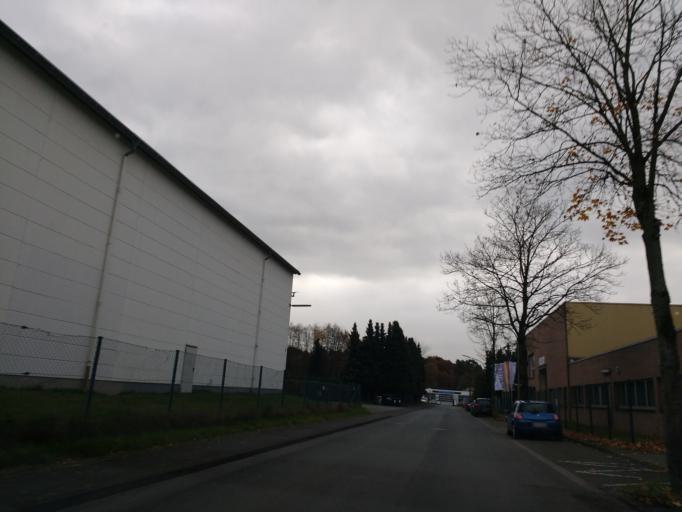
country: DE
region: North Rhine-Westphalia
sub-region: Regierungsbezirk Detmold
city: Hovelhof
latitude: 51.7690
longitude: 8.7026
